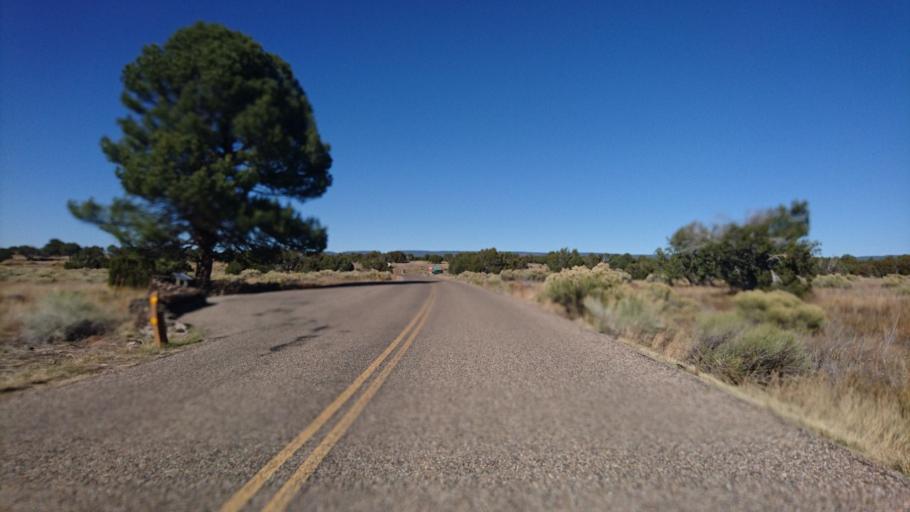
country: US
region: New Mexico
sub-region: McKinley County
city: Thoreau
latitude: 35.0415
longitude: -108.3382
